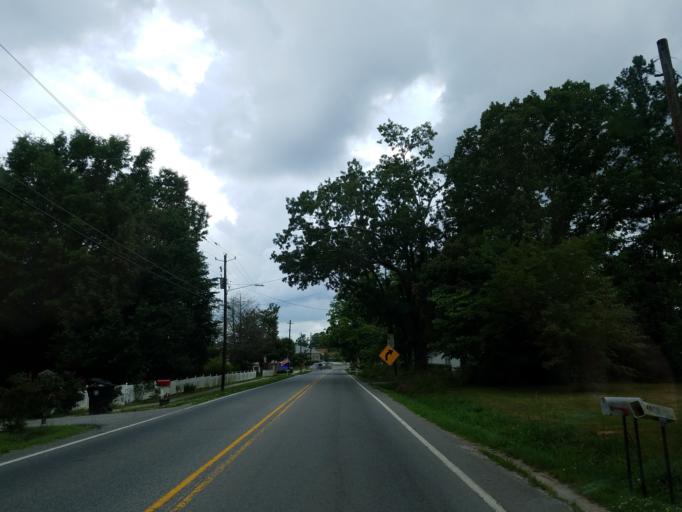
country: US
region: Georgia
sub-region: Dawson County
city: Dawsonville
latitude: 34.4224
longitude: -84.1105
